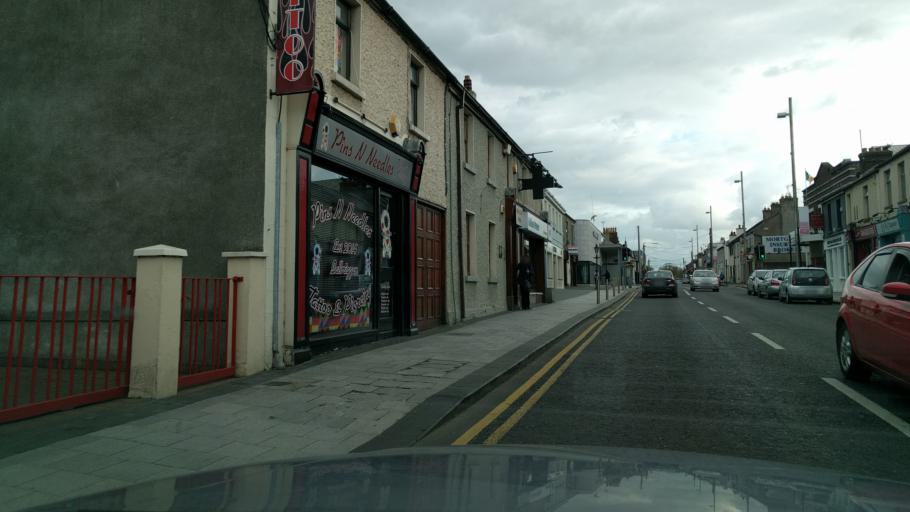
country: IE
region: Leinster
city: Balbriggan
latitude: 53.6081
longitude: -6.1832
